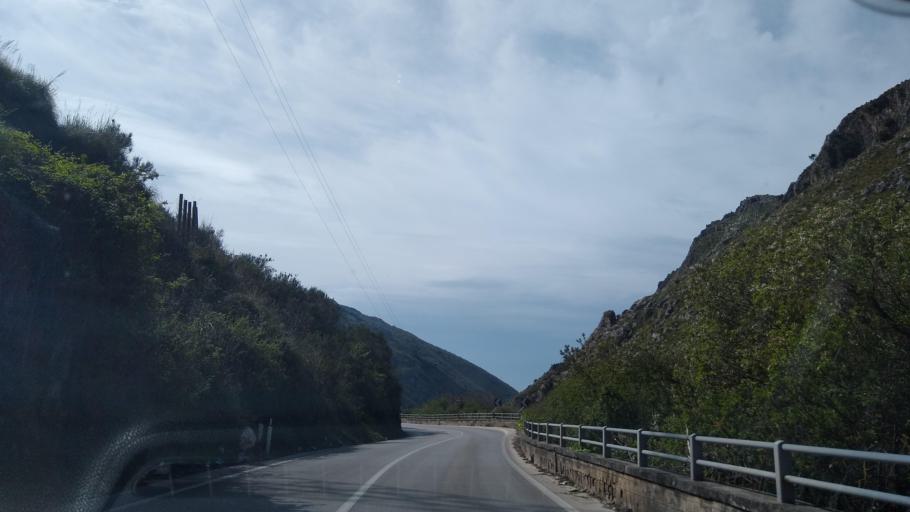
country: IT
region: Sicily
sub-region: Palermo
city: Pioppo
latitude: 38.0490
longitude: 13.1953
